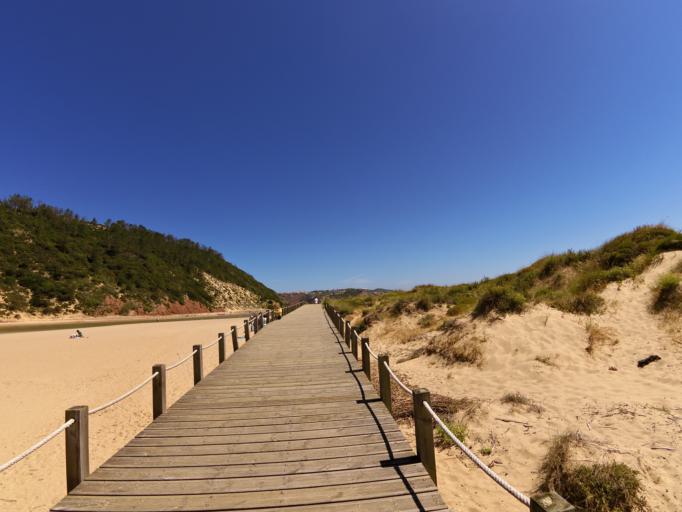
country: PT
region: Leiria
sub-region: Caldas da Rainha
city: Caldas da Rainha
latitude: 39.5034
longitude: -9.1488
